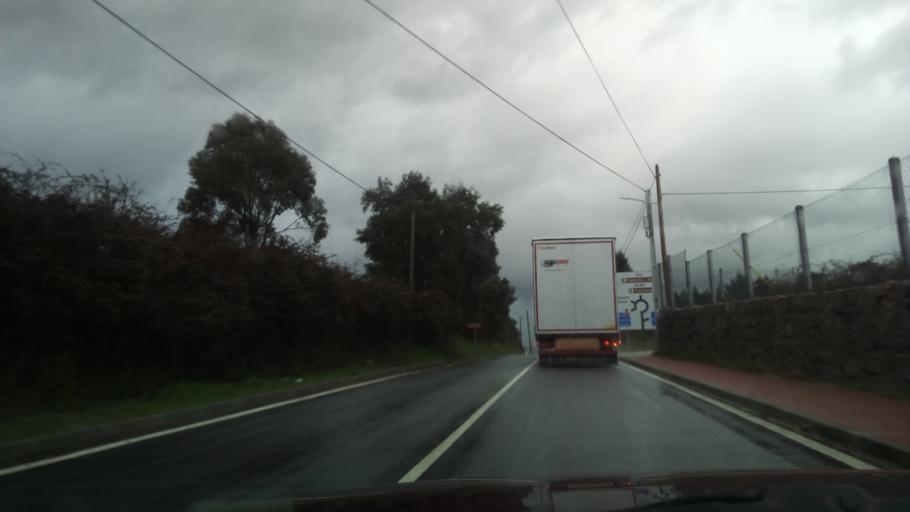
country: PT
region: Guarda
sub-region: Celorico da Beira
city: Celorico da Beira
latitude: 40.6338
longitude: -7.3473
